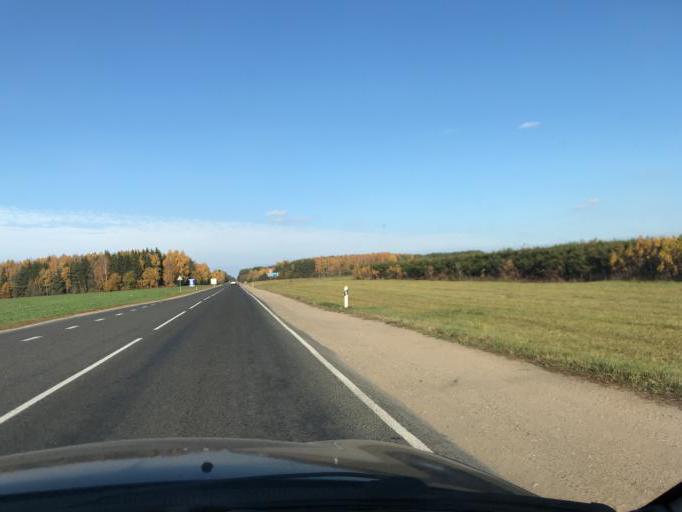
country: BY
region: Grodnenskaya
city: Lida
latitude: 53.9511
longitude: 25.2485
